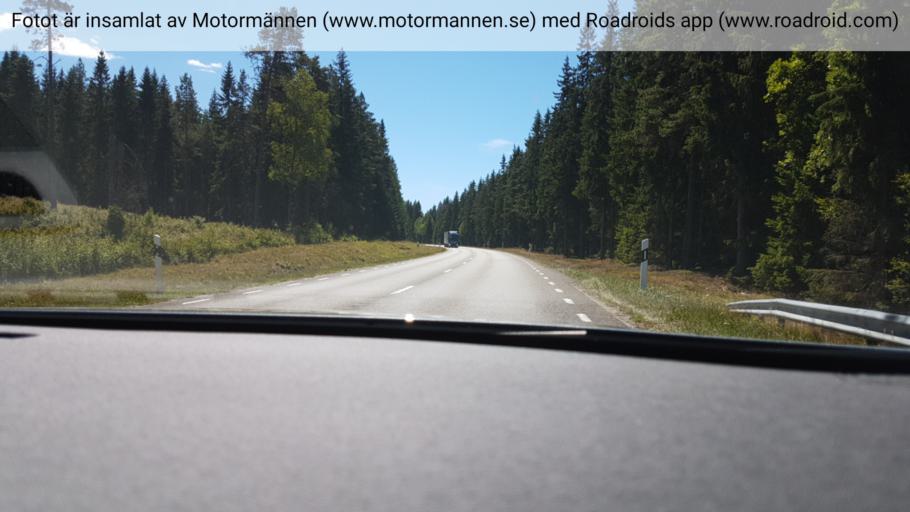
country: SE
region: Joenkoeping
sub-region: Gnosjo Kommun
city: Marieholm
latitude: 57.6292
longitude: 13.7779
